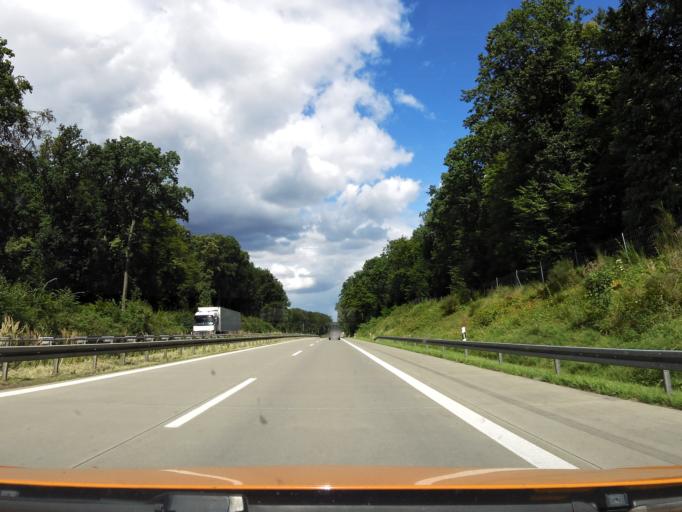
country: DE
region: Brandenburg
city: Althuttendorf
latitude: 52.9879
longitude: 13.8207
